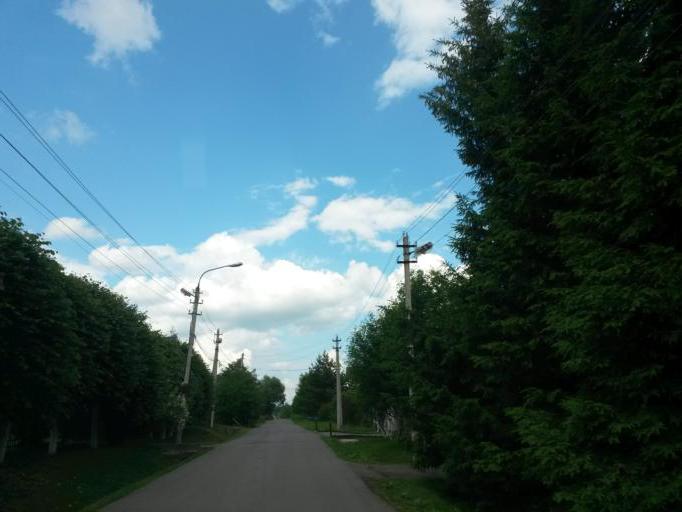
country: RU
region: Moskovskaya
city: Lyubuchany
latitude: 55.2652
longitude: 37.5558
